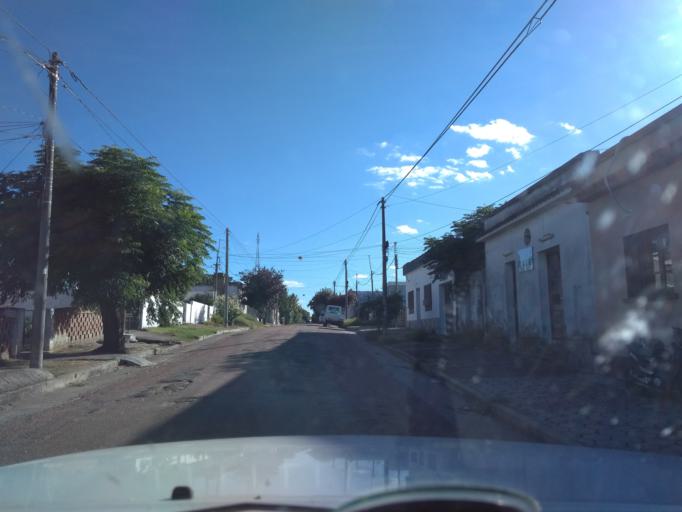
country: UY
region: Florida
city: Florida
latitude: -34.0938
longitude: -56.2089
